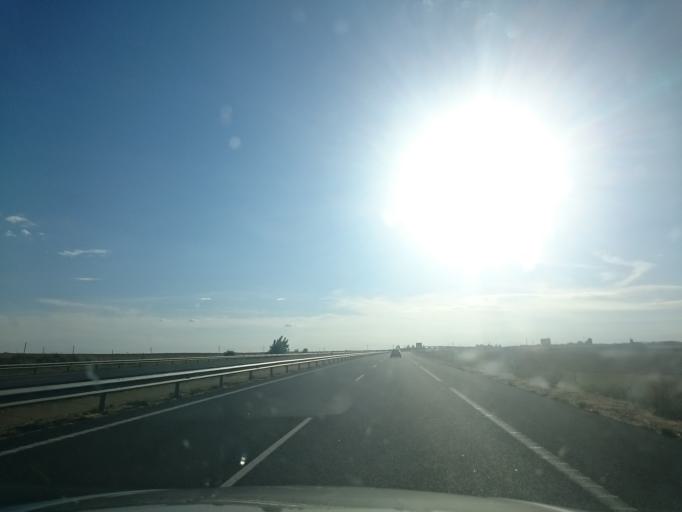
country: ES
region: Castille and Leon
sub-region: Provincia de Palencia
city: Osornillo
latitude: 42.4010
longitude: -4.3364
